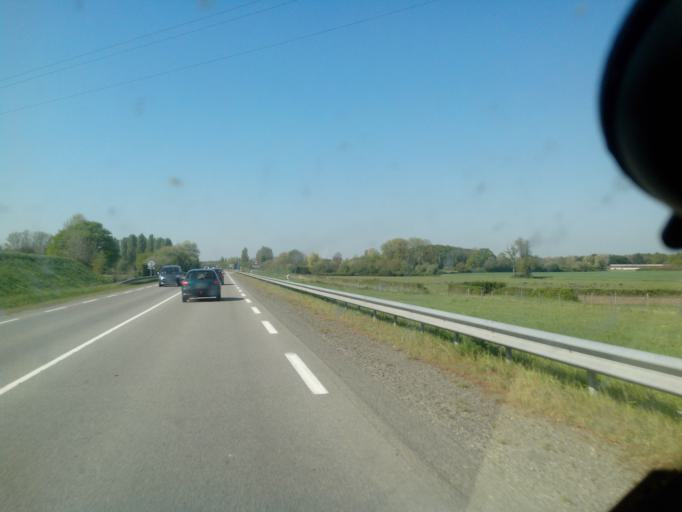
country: FR
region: Pays de la Loire
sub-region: Departement de la Loire-Atlantique
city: Arthon-en-Retz
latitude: 47.1213
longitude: -1.9406
